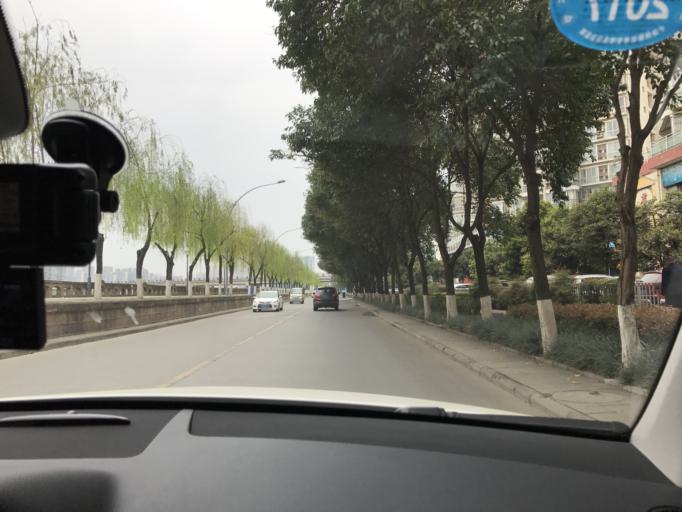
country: CN
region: Sichuan
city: Mianyang
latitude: 31.4539
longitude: 104.7092
